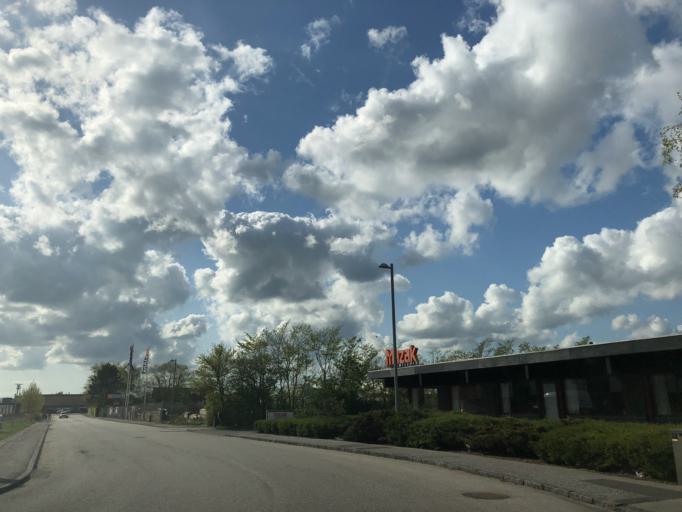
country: DK
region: Zealand
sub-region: Ringsted Kommune
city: Ringsted
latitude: 55.4356
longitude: 11.7949
